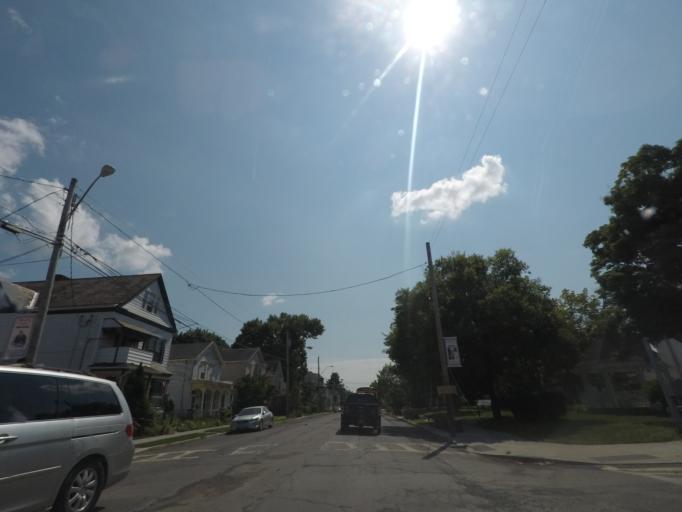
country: US
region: New York
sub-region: Albany County
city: Watervliet
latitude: 42.7130
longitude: -73.7074
